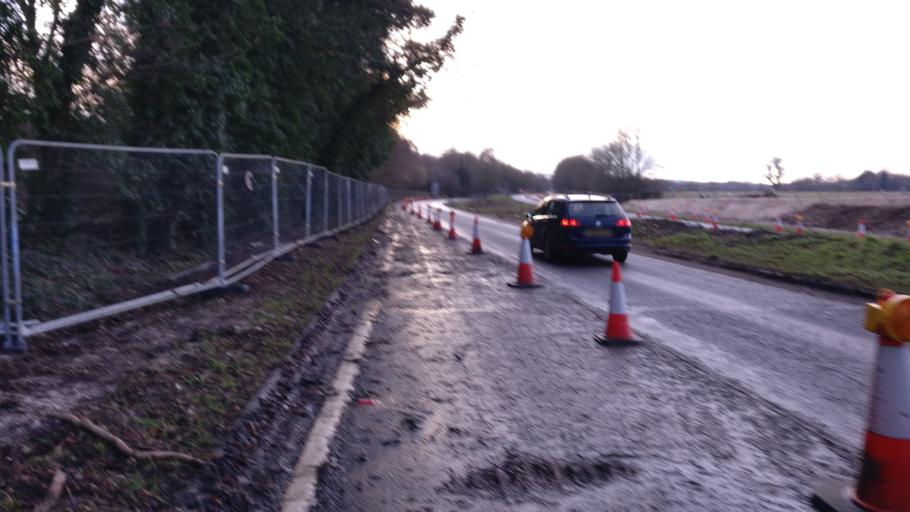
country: GB
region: England
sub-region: Hampshire
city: Basingstoke
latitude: 51.2271
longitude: -1.1509
